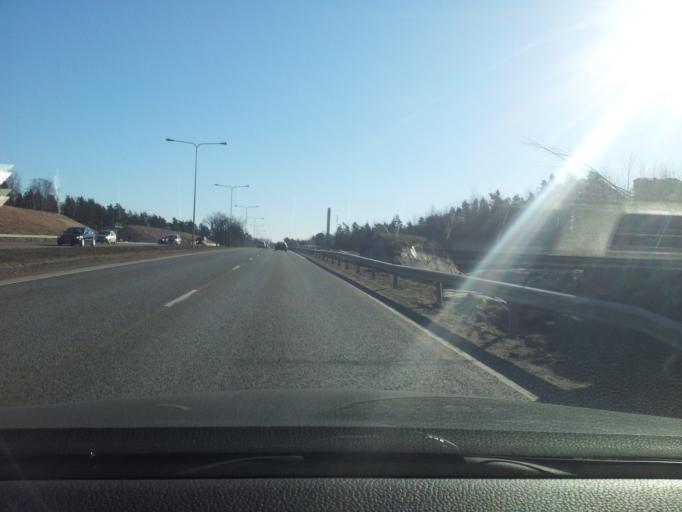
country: FI
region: Uusimaa
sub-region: Helsinki
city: Vantaa
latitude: 60.2294
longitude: 25.0581
